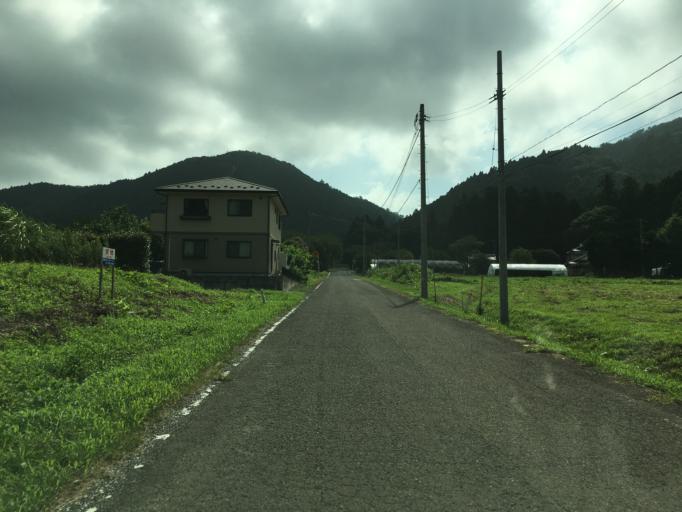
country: JP
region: Miyagi
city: Marumori
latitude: 37.8899
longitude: 140.8738
